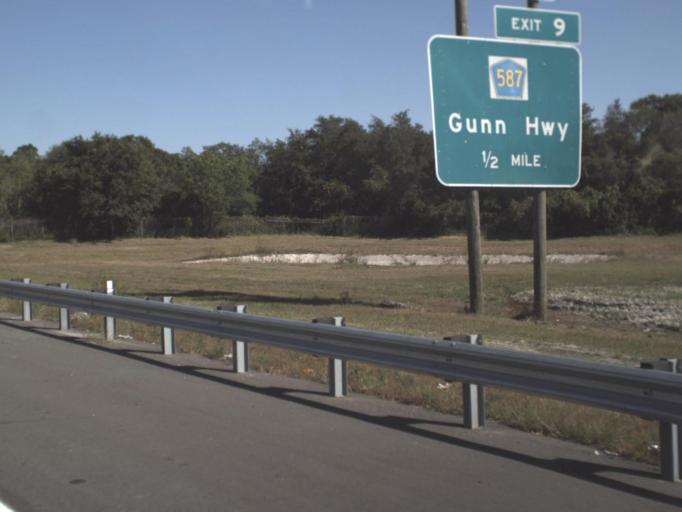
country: US
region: Florida
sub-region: Hillsborough County
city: Citrus Park
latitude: 28.0567
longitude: -82.5696
